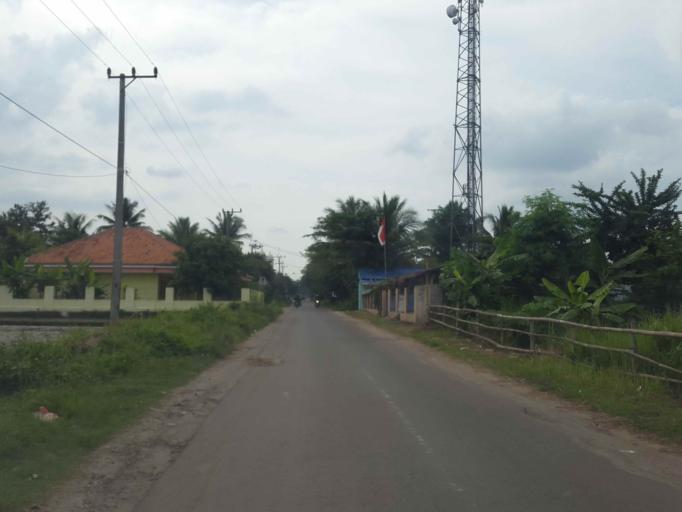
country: ID
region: Banten
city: Panyirapan
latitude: -6.2192
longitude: 106.2031
